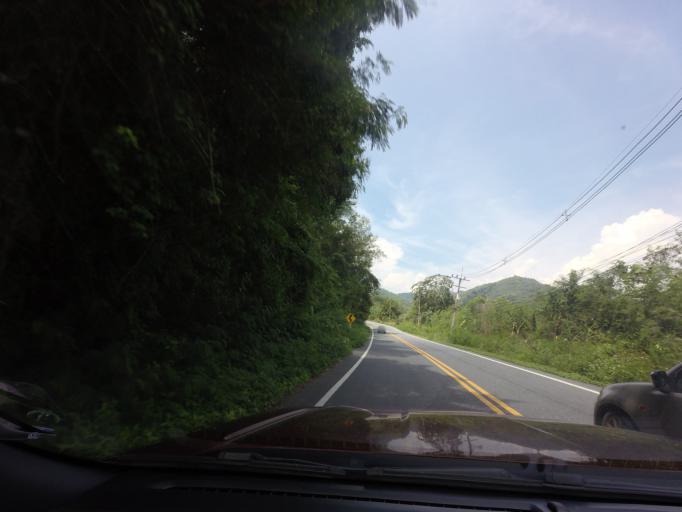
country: TH
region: Yala
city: Than To
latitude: 6.0357
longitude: 101.2094
